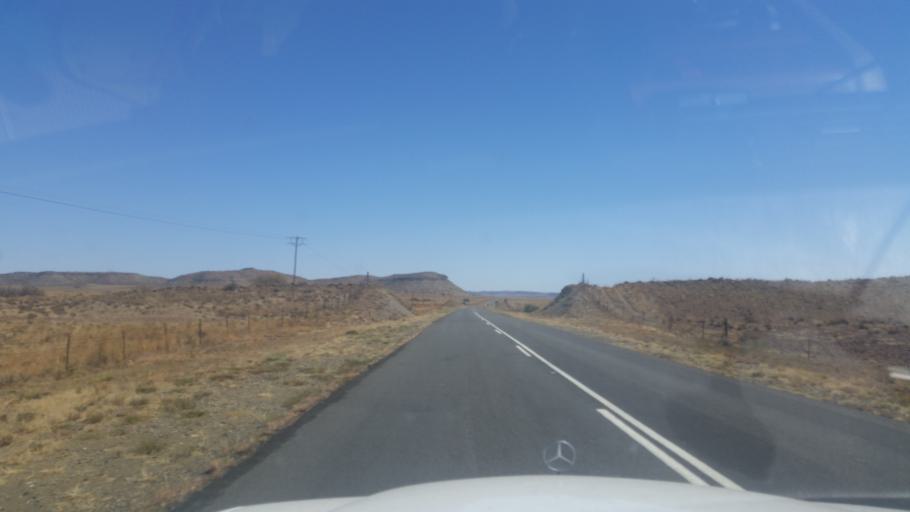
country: ZA
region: Northern Cape
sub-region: Pixley ka Seme District Municipality
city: Colesberg
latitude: -30.7539
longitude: 25.7109
